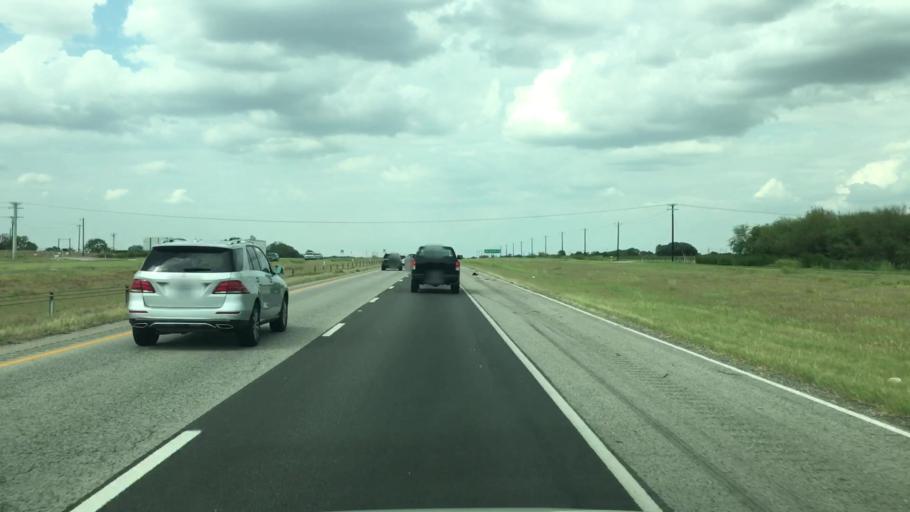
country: US
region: Texas
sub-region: Atascosa County
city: Pleasanton
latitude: 29.0070
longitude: -98.4310
